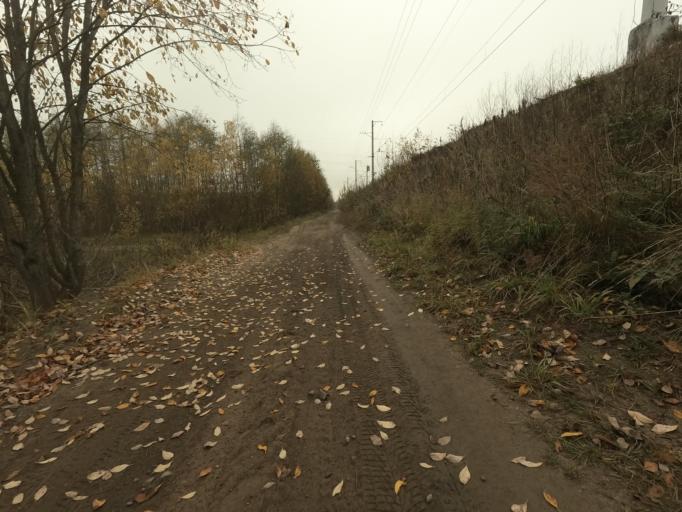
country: RU
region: Leningrad
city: Pavlovo
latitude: 59.7781
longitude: 30.8994
